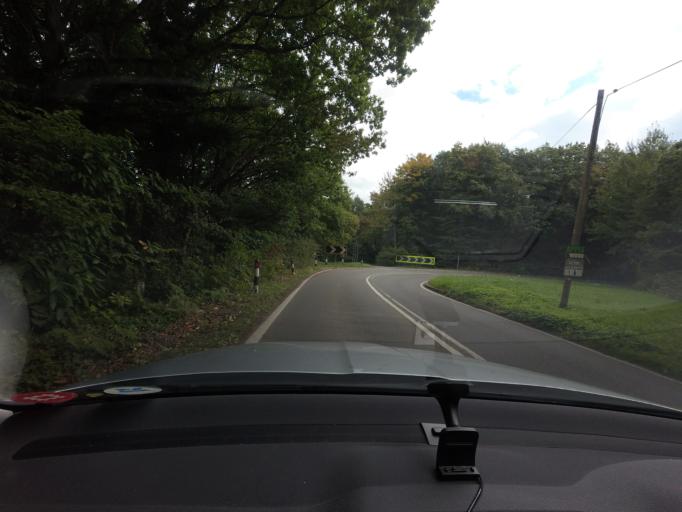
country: GB
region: England
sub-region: Kent
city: Tonbridge
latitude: 51.2294
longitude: 0.2931
